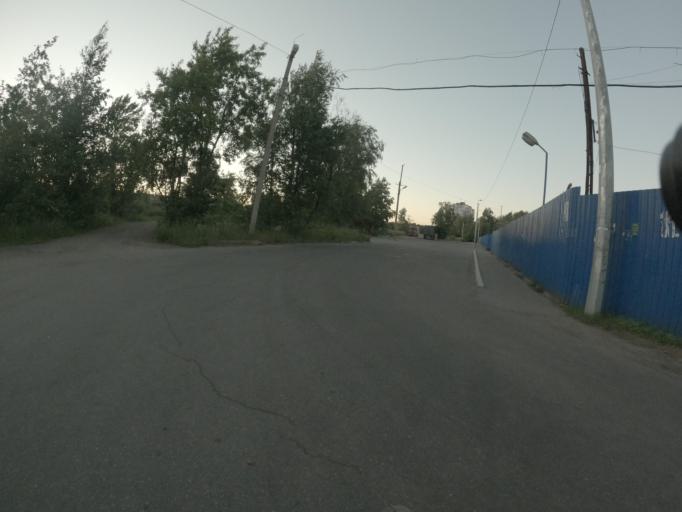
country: RU
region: St.-Petersburg
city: Krasnogvargeisky
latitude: 59.9830
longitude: 30.5156
